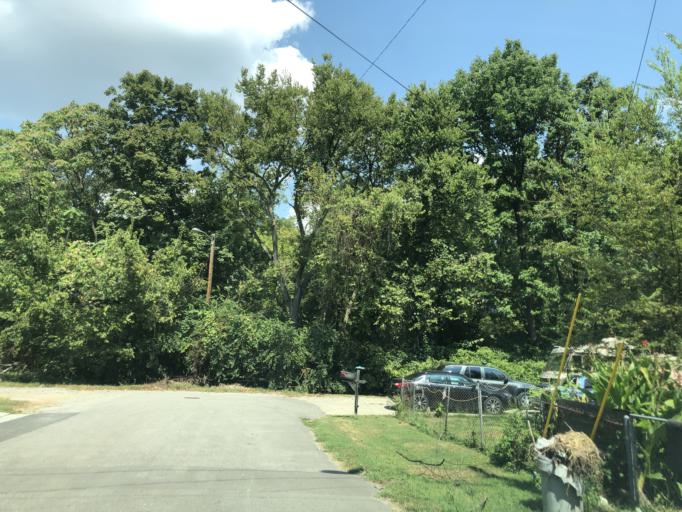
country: US
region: Tennessee
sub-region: Davidson County
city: Nashville
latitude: 36.1293
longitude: -86.7465
